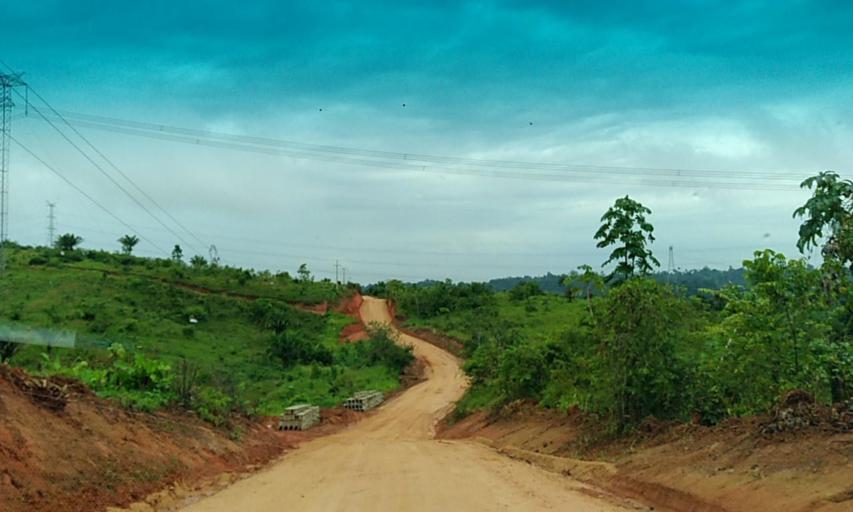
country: BR
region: Para
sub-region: Altamira
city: Altamira
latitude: -3.1017
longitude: -51.6341
